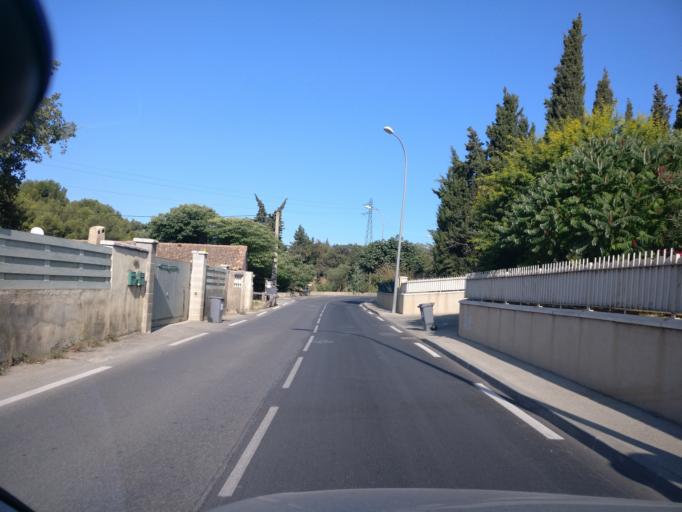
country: FR
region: Provence-Alpes-Cote d'Azur
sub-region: Departement du Var
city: Sanary-sur-Mer
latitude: 43.1306
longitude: 5.8161
